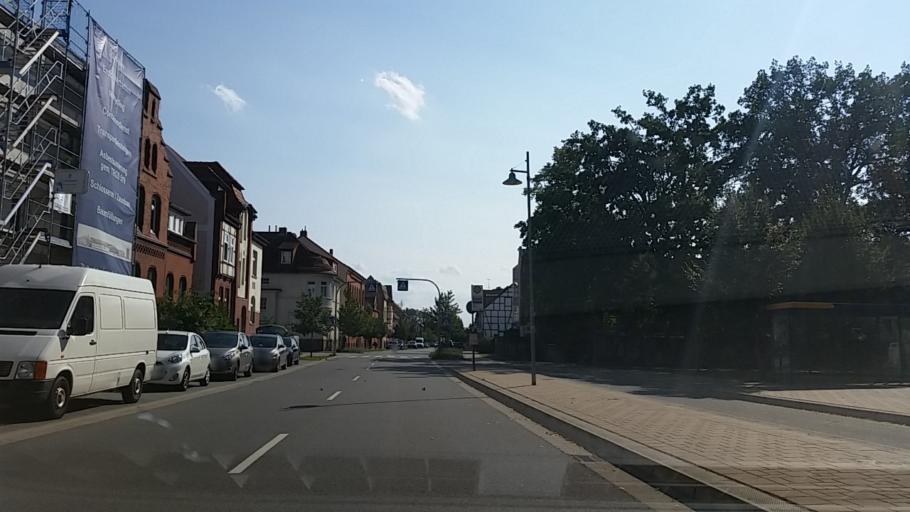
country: DE
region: Saxony-Anhalt
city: Salzwedel
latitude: 52.8473
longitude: 11.1515
